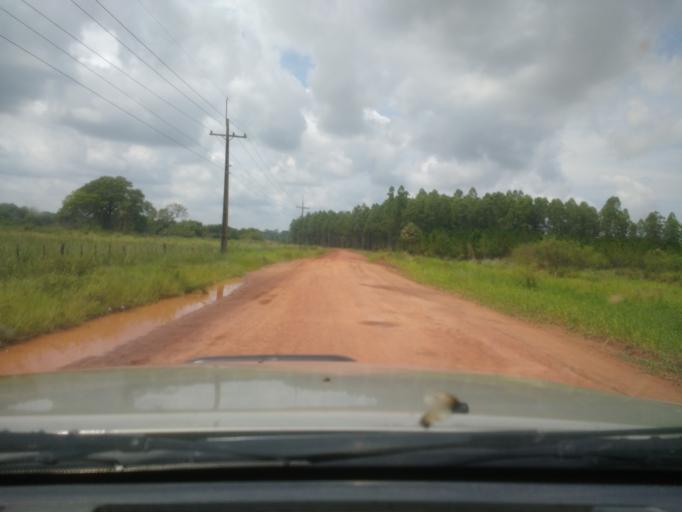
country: PY
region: San Pedro
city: Puerto Rosario
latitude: -24.4012
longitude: -57.1041
